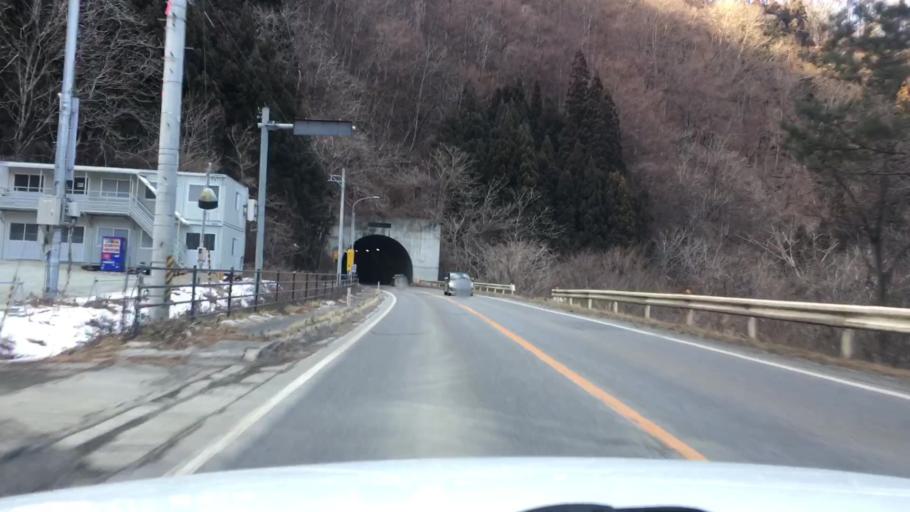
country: JP
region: Iwate
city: Tono
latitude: 39.6210
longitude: 141.6201
